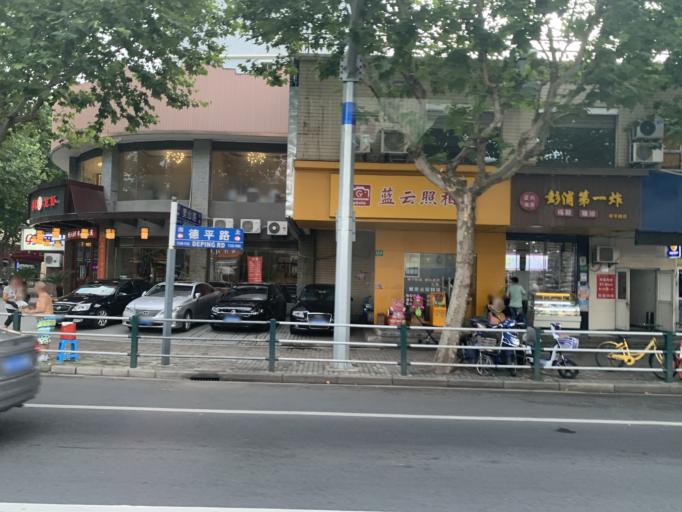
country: CN
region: Shanghai Shi
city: Pudong
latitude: 31.2432
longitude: 121.5647
